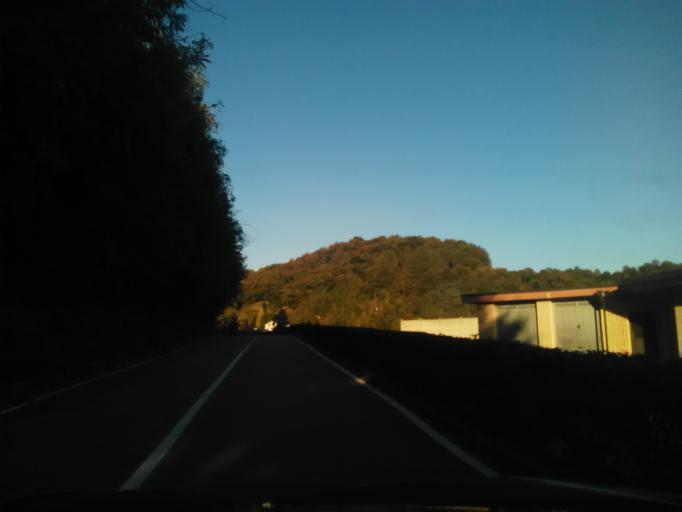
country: IT
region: Piedmont
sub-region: Provincia di Vercelli
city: Borgosesia
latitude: 45.7193
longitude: 8.2802
